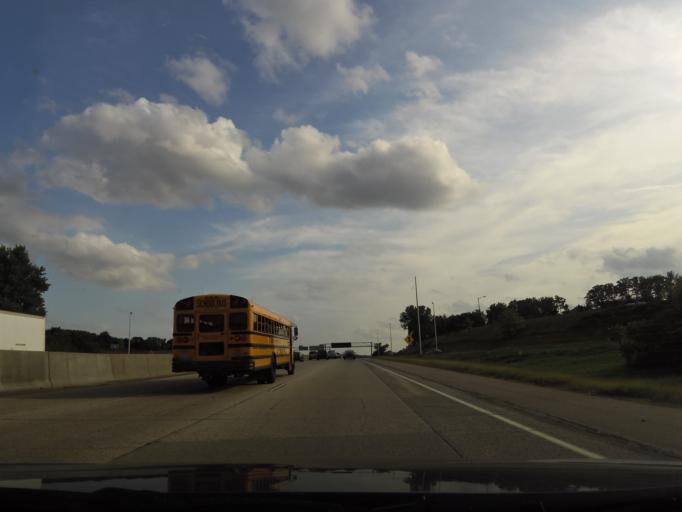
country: US
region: Minnesota
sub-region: Dakota County
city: Burnsville
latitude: 44.7300
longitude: -93.2831
